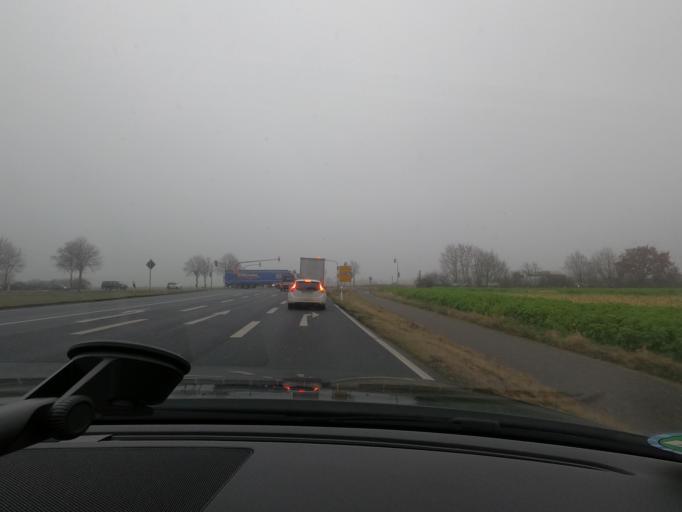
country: DE
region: North Rhine-Westphalia
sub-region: Regierungsbezirk Koln
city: Merzenich
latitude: 50.8236
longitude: 6.5421
